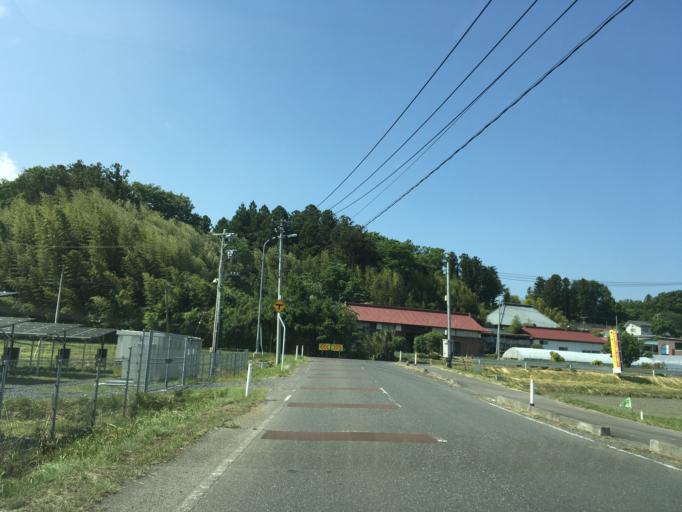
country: JP
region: Miyagi
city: Wakuya
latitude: 38.6675
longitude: 141.1577
